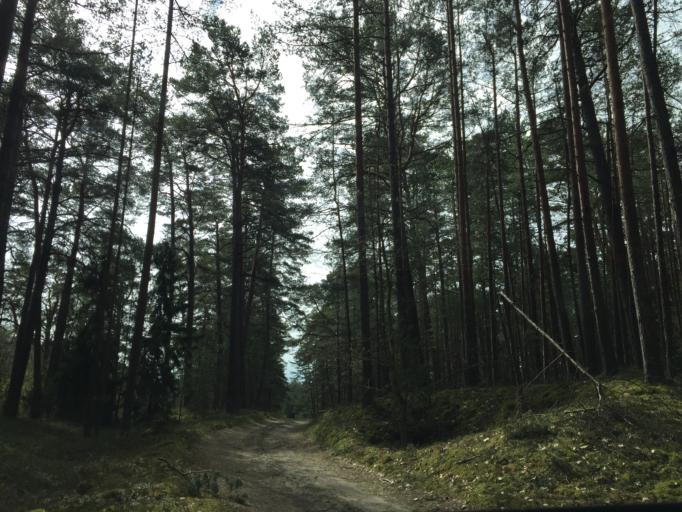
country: LV
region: Salacgrivas
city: Salacgriva
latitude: 57.6887
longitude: 24.3611
